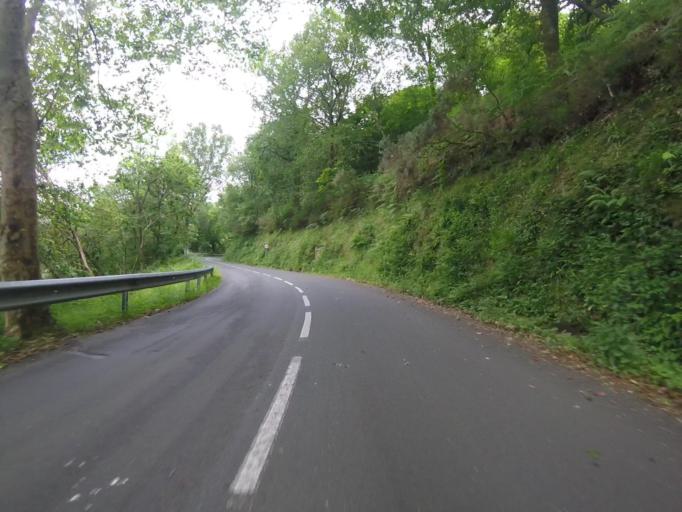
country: ES
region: Basque Country
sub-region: Provincia de Guipuzcoa
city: Errenteria
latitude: 43.2753
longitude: -1.8492
